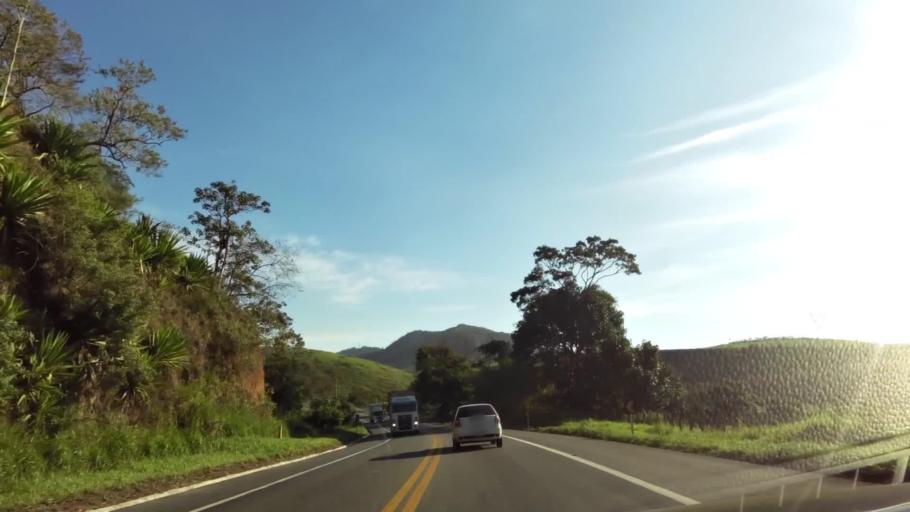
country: BR
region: Espirito Santo
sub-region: Viana
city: Viana
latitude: -20.4030
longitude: -40.4556
